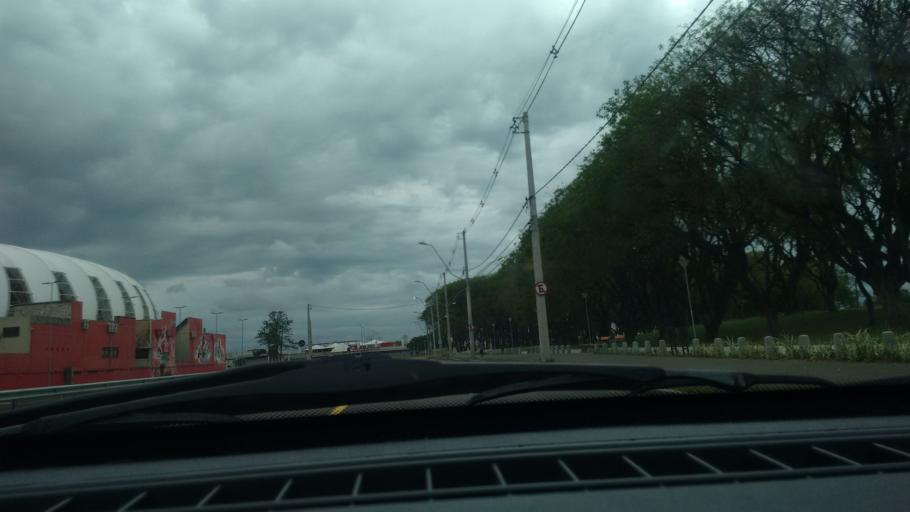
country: BR
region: Rio Grande do Sul
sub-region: Porto Alegre
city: Porto Alegre
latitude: -30.0636
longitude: -51.2336
